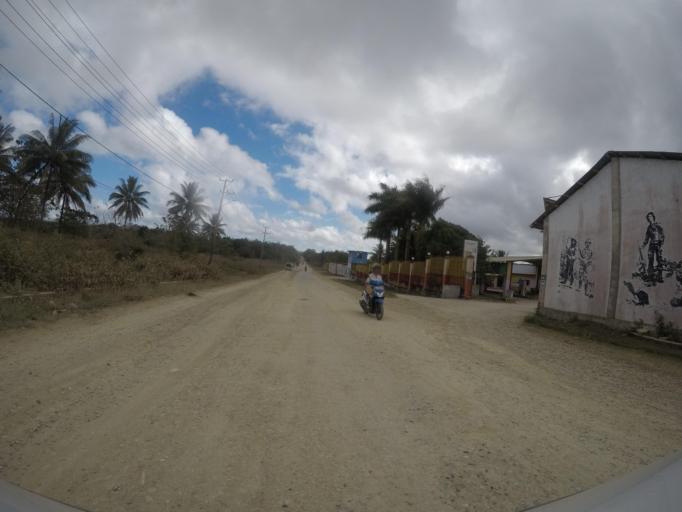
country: TL
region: Lautem
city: Lospalos
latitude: -8.4912
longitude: 126.9926
